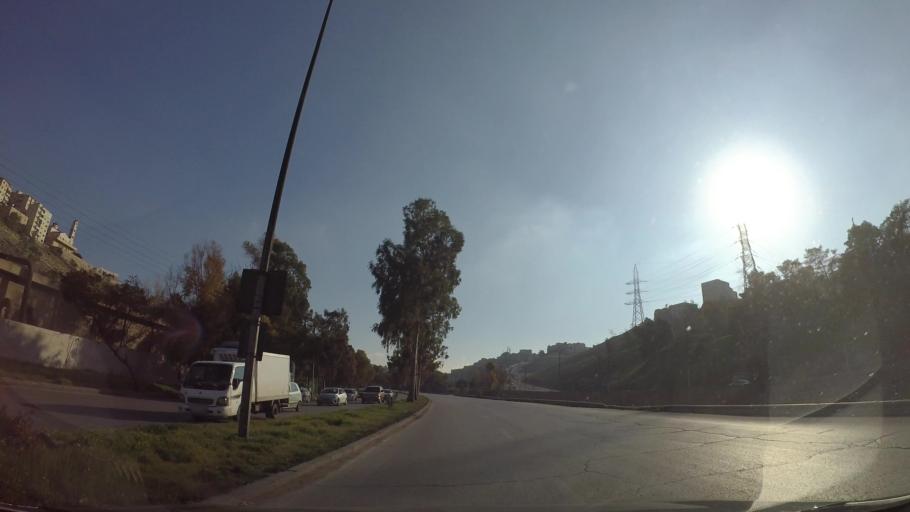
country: JO
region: Amman
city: Amman
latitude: 31.9799
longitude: 35.9731
